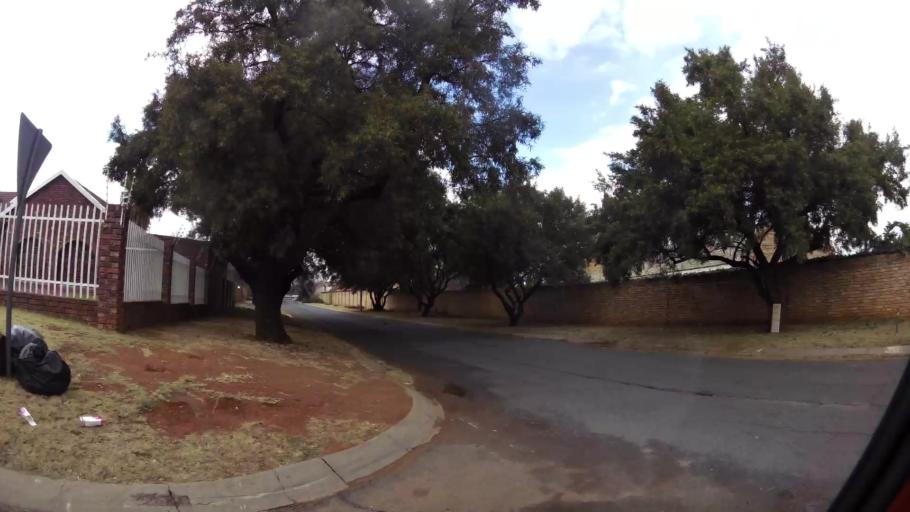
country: ZA
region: Gauteng
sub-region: Sedibeng District Municipality
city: Vanderbijlpark
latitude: -26.7367
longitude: 27.8520
